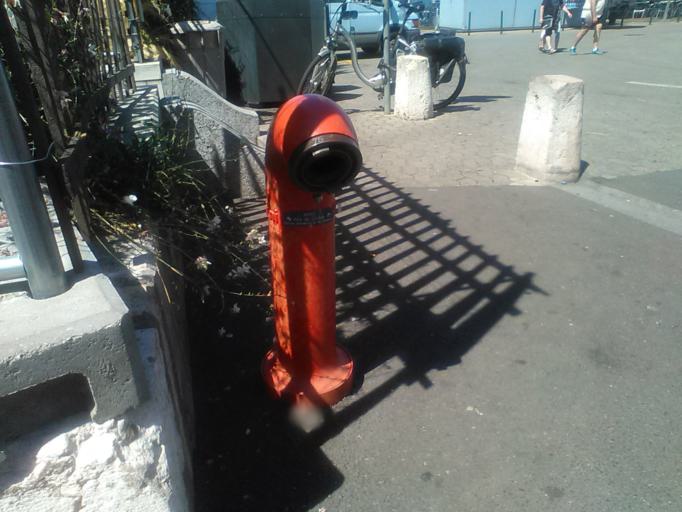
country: CH
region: Geneva
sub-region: Geneva
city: Geneve
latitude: 46.2052
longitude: 6.1539
